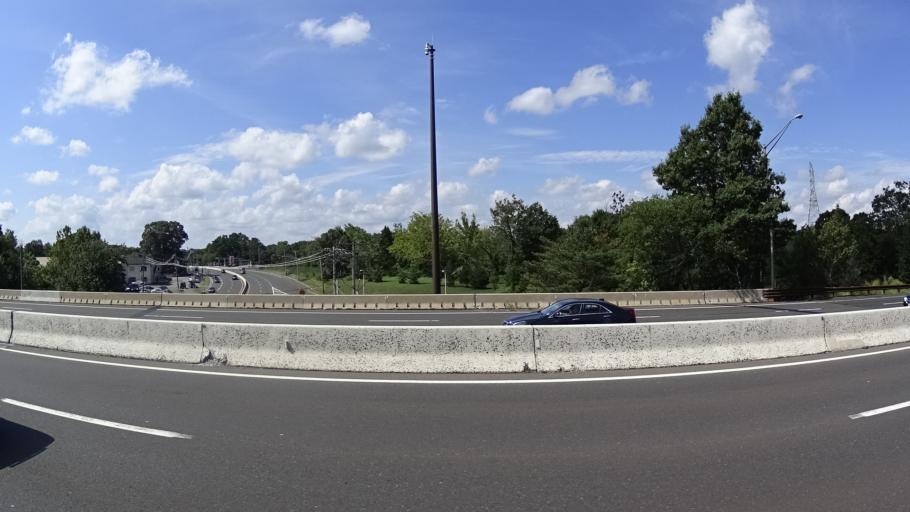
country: US
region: New Jersey
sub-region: Middlesex County
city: South Amboy
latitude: 40.4716
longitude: -74.2963
